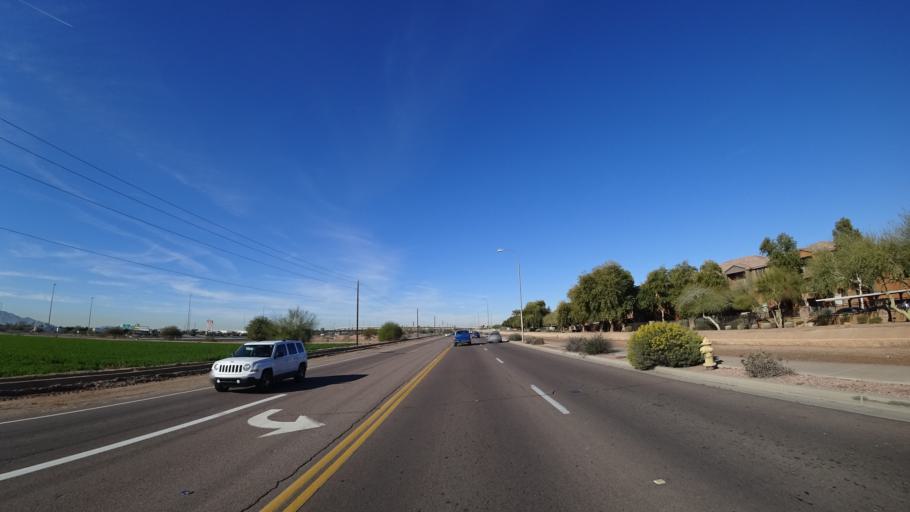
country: US
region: Arizona
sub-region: Maricopa County
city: Tolleson
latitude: 33.4650
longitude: -112.2583
